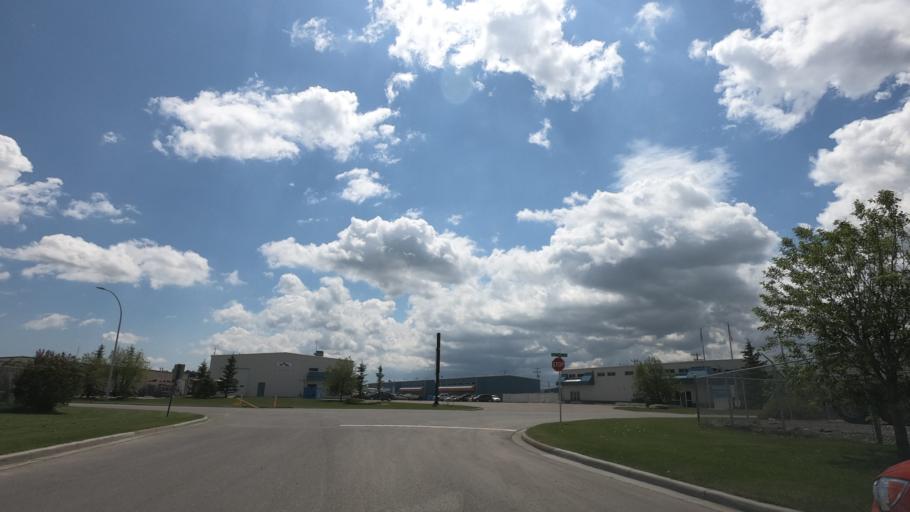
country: CA
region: Alberta
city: Airdrie
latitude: 51.2938
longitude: -113.9944
